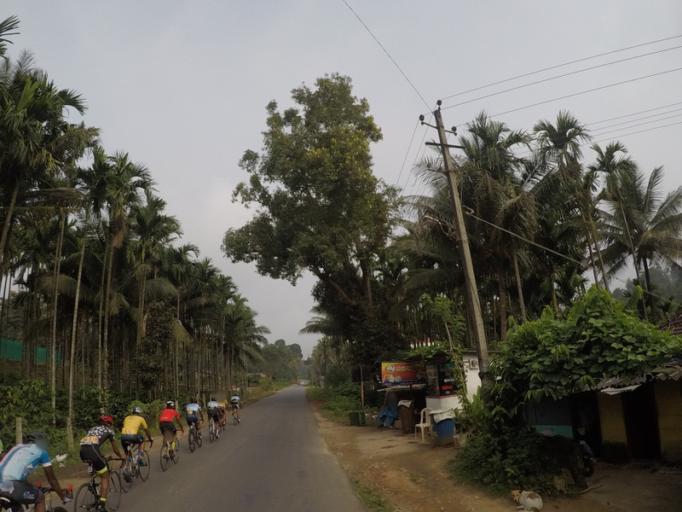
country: IN
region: Karnataka
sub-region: Chikmagalur
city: Chikmagalur
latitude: 13.3563
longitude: 75.5358
